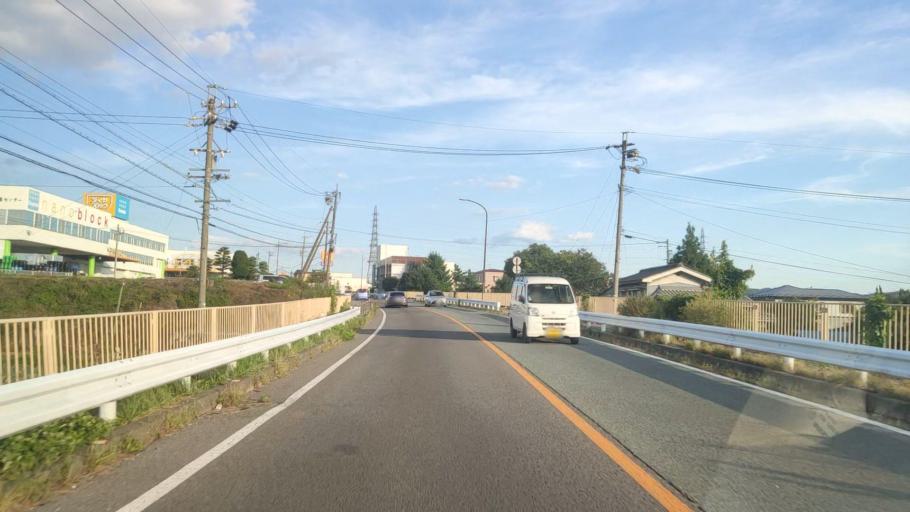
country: JP
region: Nagano
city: Kamimaruko
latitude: 36.3531
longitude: 138.3498
